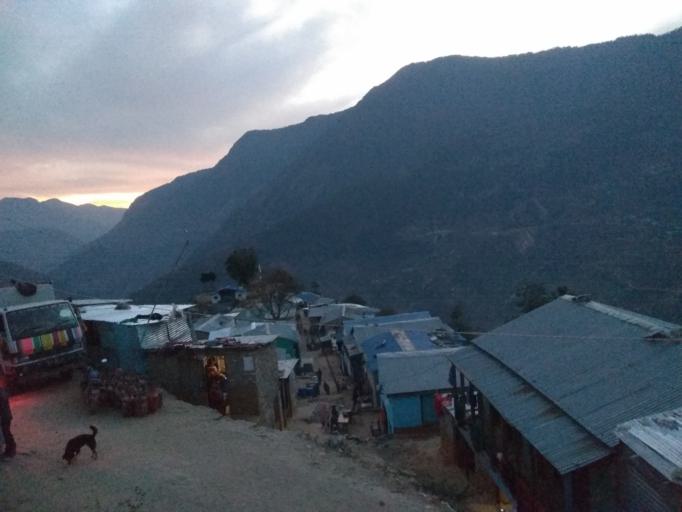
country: NP
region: Far Western
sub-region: Seti Zone
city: Achham
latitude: 29.2392
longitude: 81.6380
